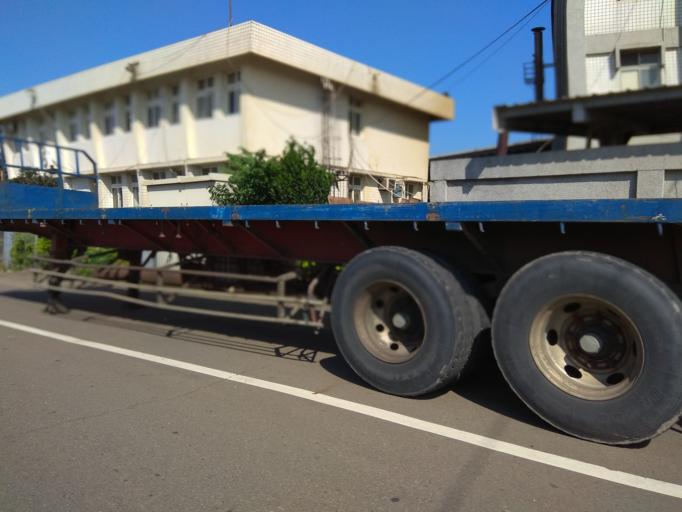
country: TW
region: Taiwan
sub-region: Hsinchu
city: Zhubei
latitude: 24.9808
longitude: 121.0378
